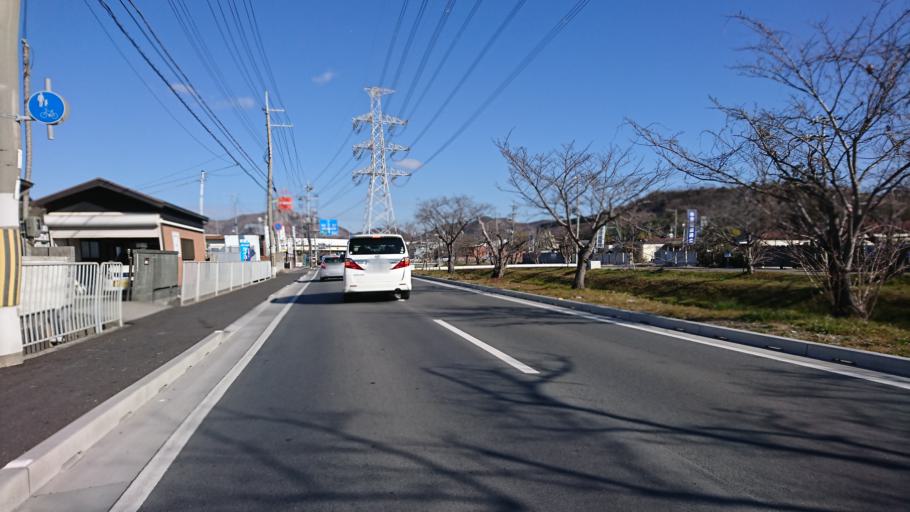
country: JP
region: Hyogo
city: Kakogawacho-honmachi
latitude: 34.7835
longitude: 134.7819
